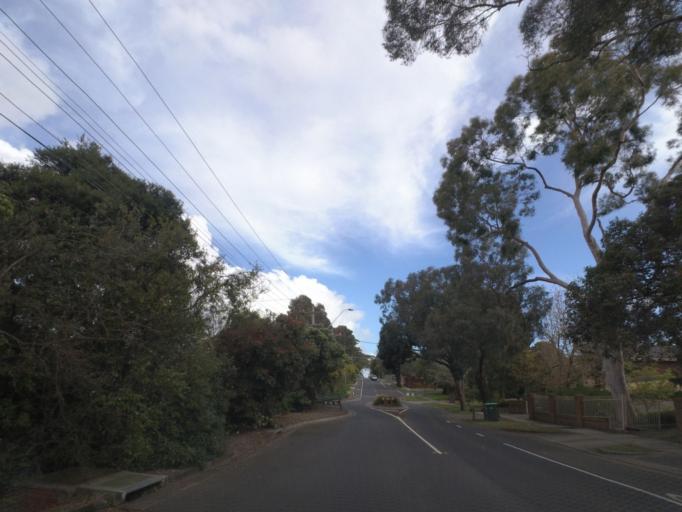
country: AU
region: Victoria
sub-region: Whitehorse
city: Vermont
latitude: -37.8413
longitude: 145.1903
